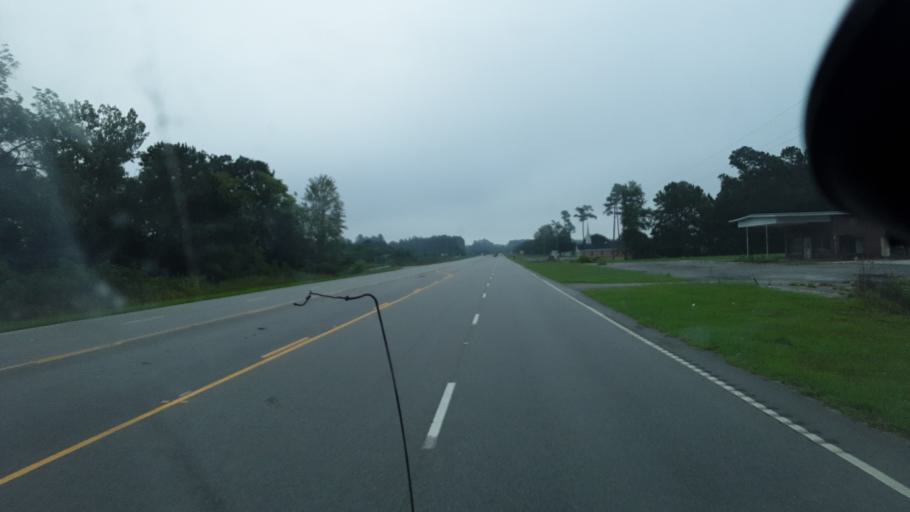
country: US
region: South Carolina
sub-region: Florence County
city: Johnsonville
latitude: 33.8824
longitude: -79.4671
